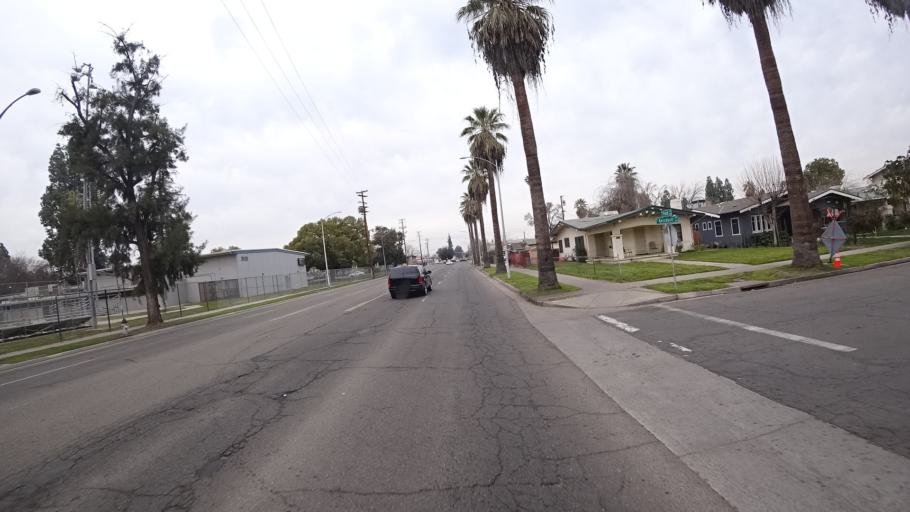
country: US
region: California
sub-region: Fresno County
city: Fresno
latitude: 36.7405
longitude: -119.7724
